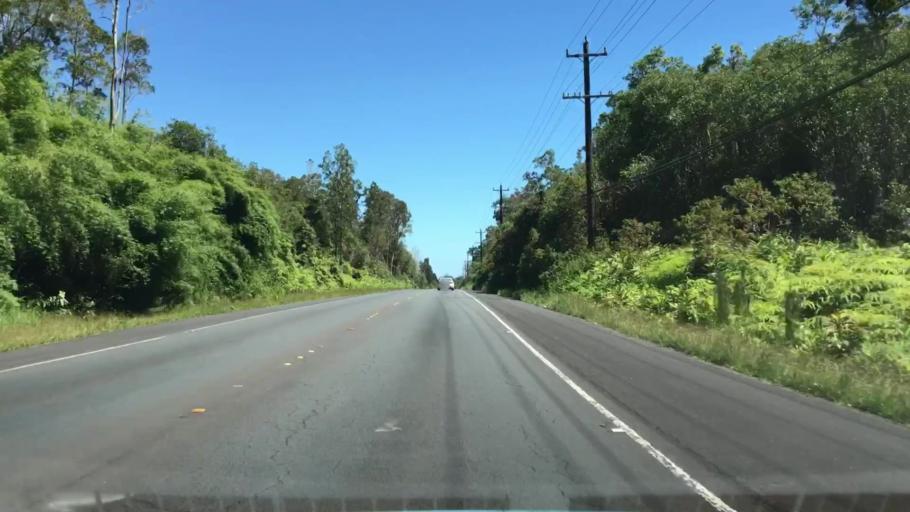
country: US
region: Hawaii
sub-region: Hawaii County
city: Mountain View
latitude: 19.5217
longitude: -155.1363
